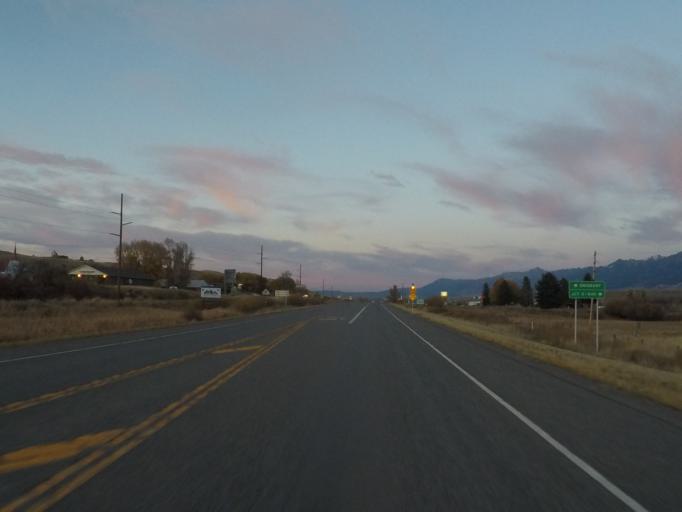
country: US
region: Montana
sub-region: Park County
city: Livingston
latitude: 45.3669
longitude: -110.7354
